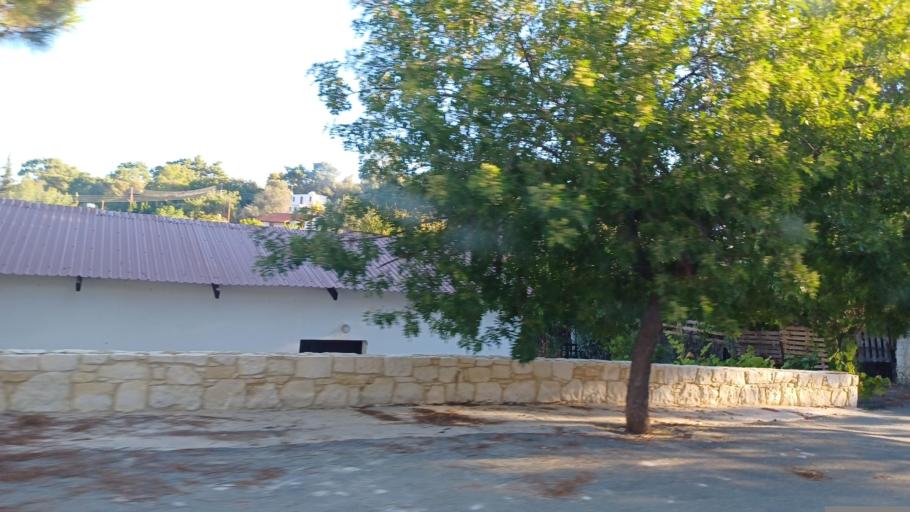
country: CY
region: Pafos
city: Polis
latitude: 34.9442
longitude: 32.5656
